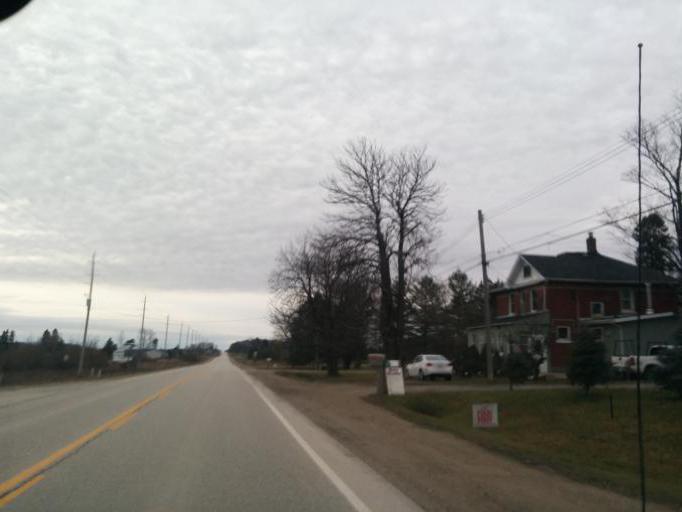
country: CA
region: Ontario
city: Shelburne
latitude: 44.0765
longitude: -80.2139
